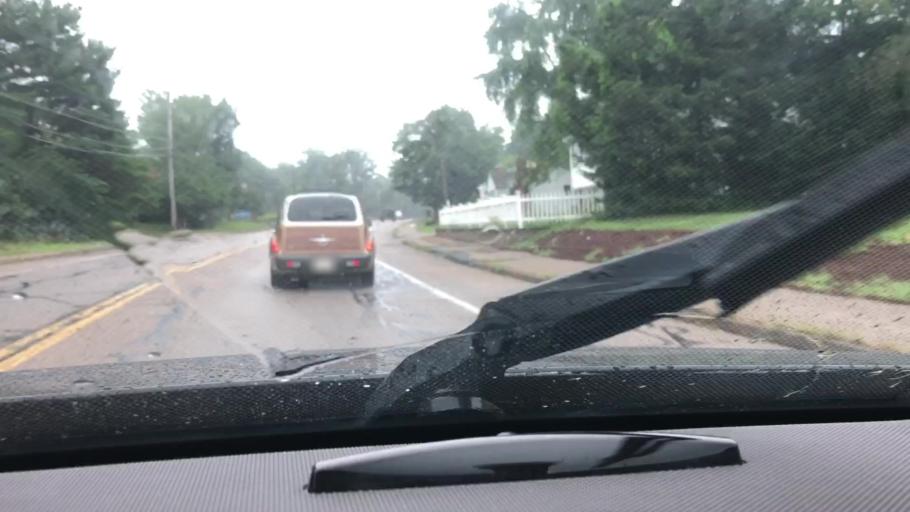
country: US
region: Massachusetts
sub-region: Norfolk County
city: Bellingham
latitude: 42.1039
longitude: -71.4731
